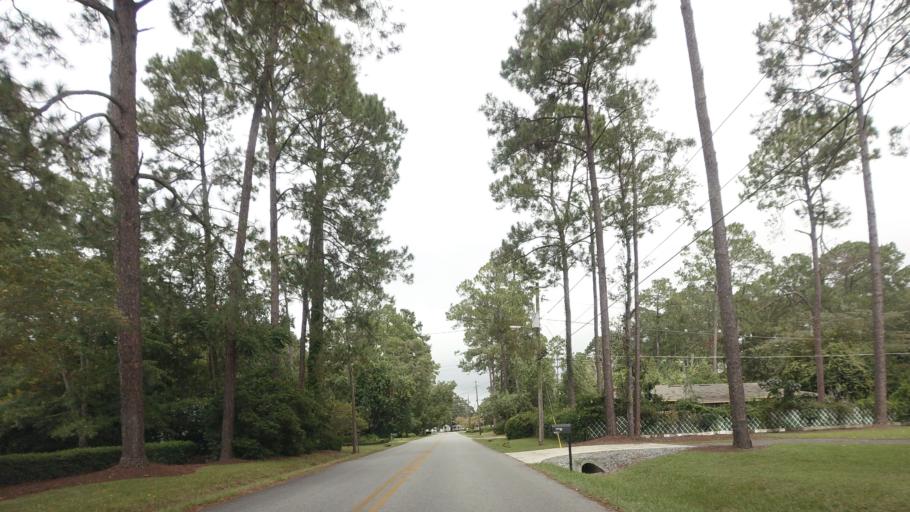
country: US
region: Georgia
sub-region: Lowndes County
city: Valdosta
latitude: 30.8578
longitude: -83.2845
